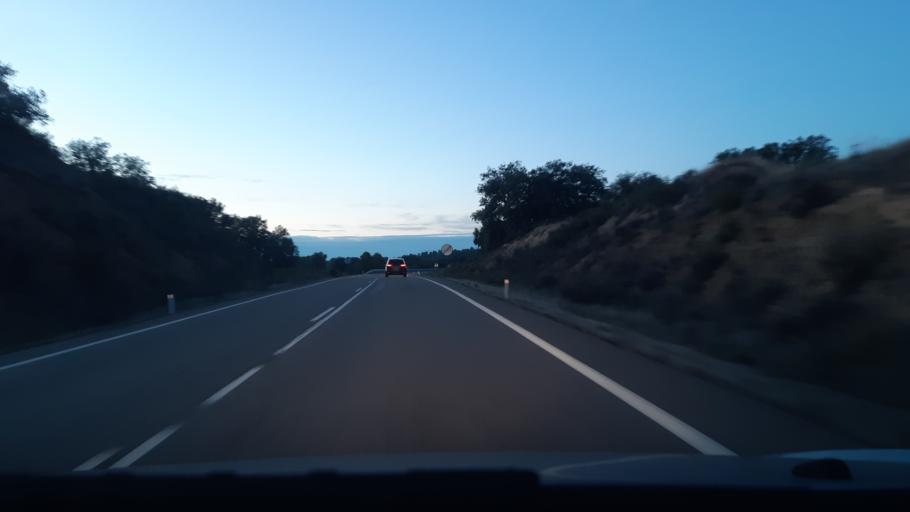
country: ES
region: Aragon
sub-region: Provincia de Teruel
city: Calaceite
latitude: 40.9727
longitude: 0.2057
